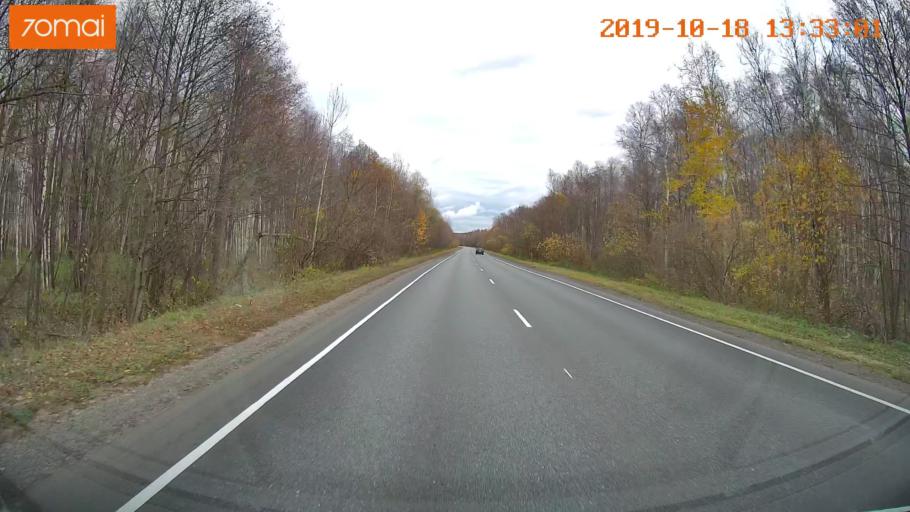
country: RU
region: Rjazan
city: Solotcha
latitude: 54.8388
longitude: 39.9273
